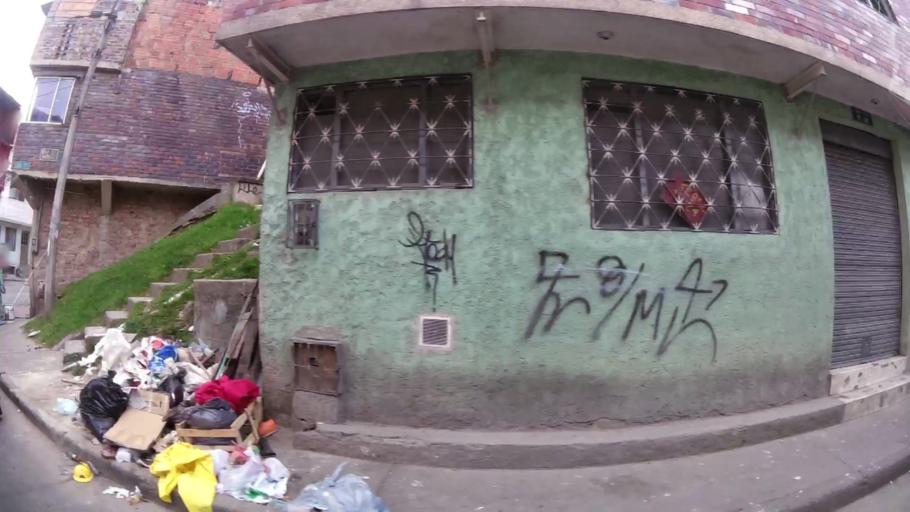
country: CO
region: Bogota D.C.
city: Bogota
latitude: 4.5816
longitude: -74.0713
